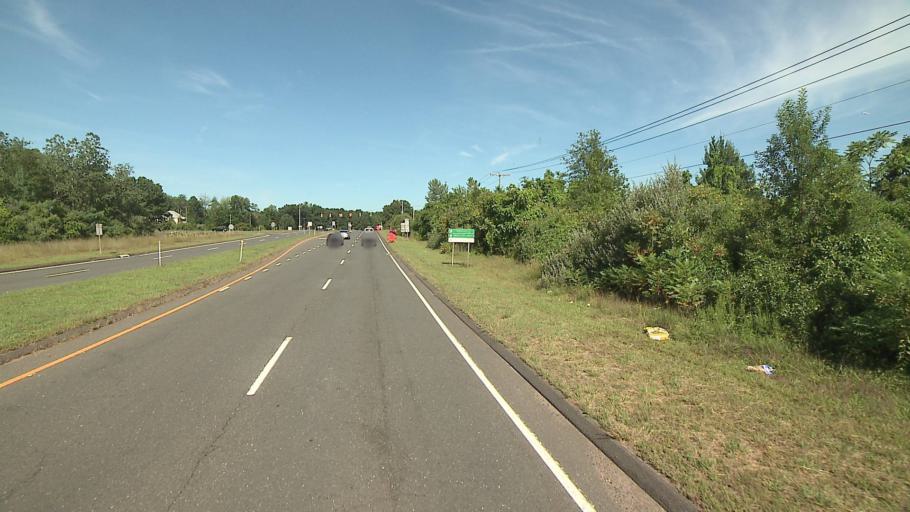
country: US
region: Connecticut
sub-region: Hartford County
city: Tariffville
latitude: 41.8819
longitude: -72.7417
